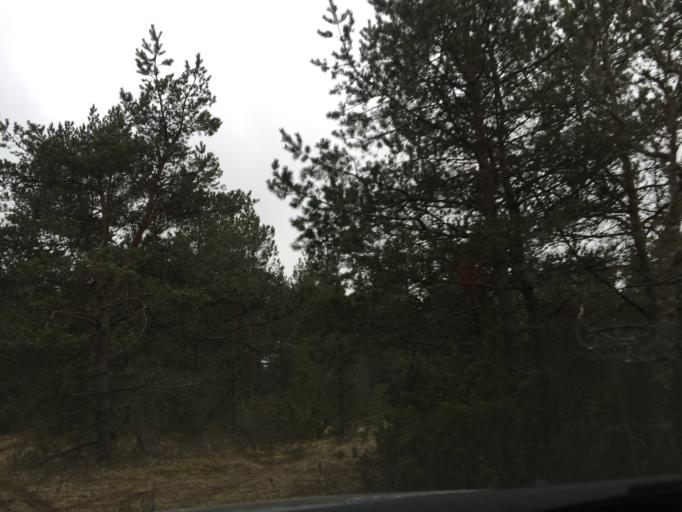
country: EE
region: Saare
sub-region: Kuressaare linn
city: Kuressaare
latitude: 58.3037
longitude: 22.2794
